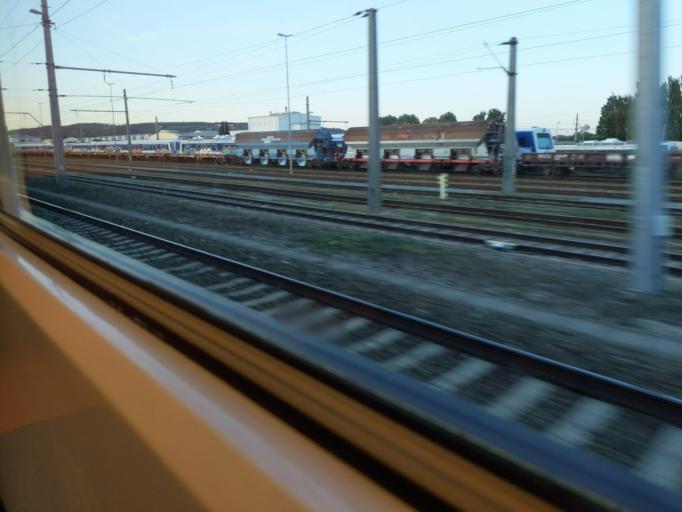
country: AT
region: Lower Austria
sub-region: Politischer Bezirk Korneuburg
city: Langenzersdorf
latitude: 48.2771
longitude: 16.3922
